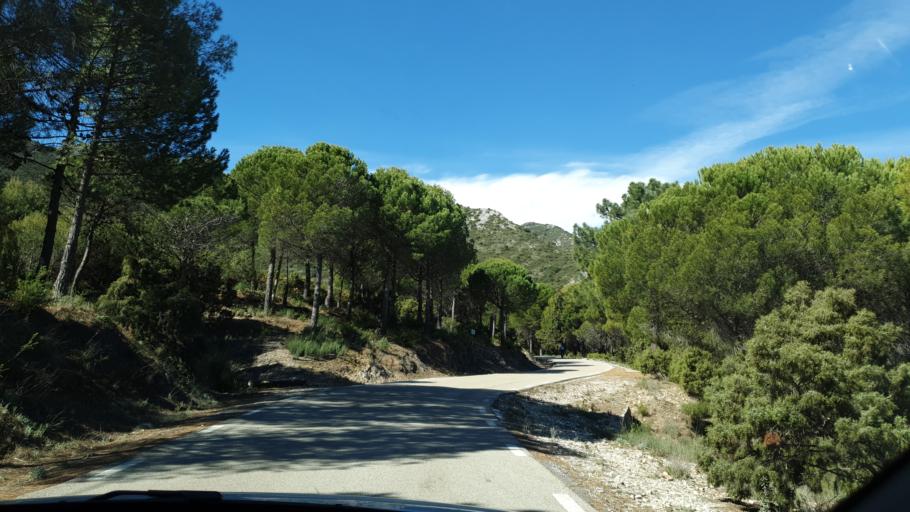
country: ES
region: Andalusia
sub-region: Provincia de Malaga
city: Ojen
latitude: 36.5873
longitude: -4.8657
